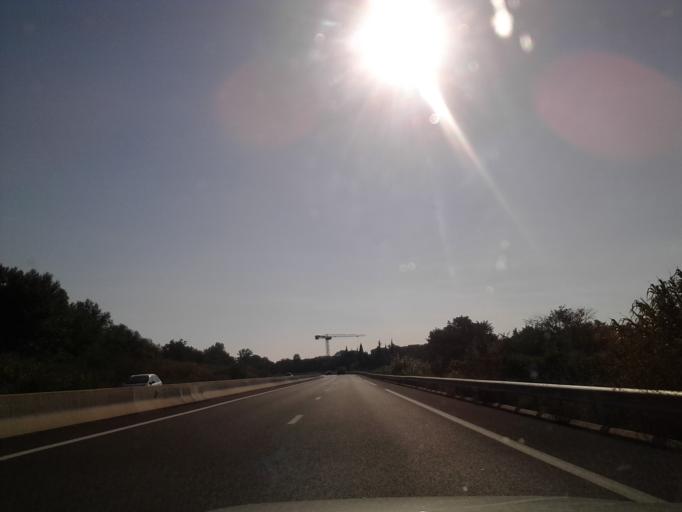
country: FR
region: Languedoc-Roussillon
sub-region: Departement des Pyrenees-Orientales
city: Ille-sur-Tet
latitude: 42.6747
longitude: 2.6188
